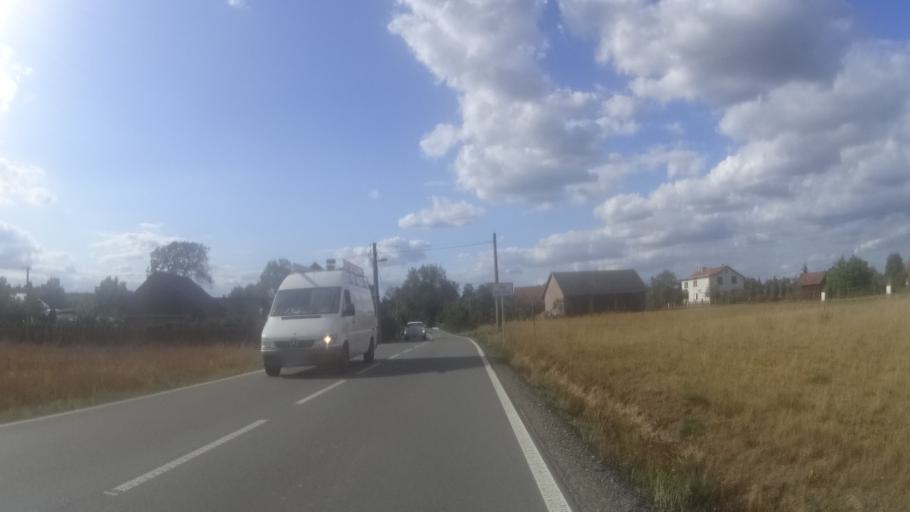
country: CZ
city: Albrechtice nad Orlici
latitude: 50.1160
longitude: 16.0717
